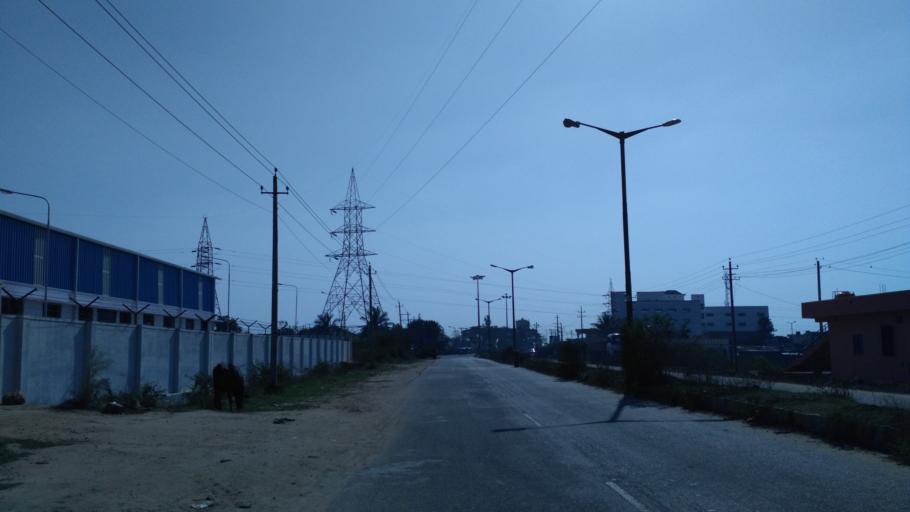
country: IN
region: Karnataka
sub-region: Hassan
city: Hassan
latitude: 12.9735
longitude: 76.1194
